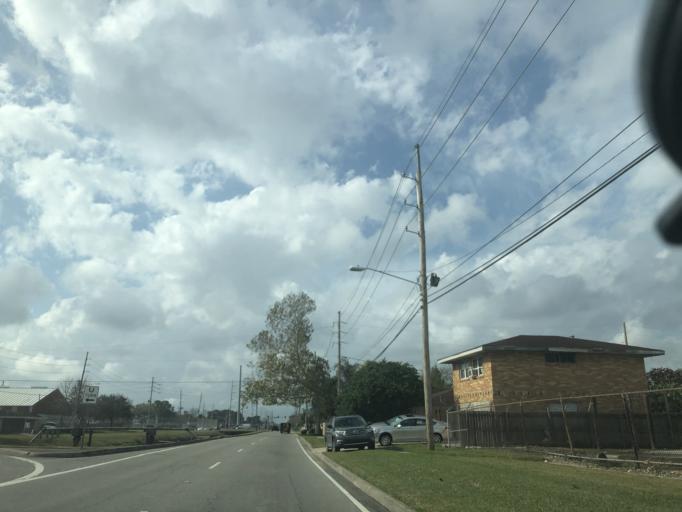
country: US
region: Louisiana
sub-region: Jefferson Parish
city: Metairie
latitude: 29.9925
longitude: -90.1568
